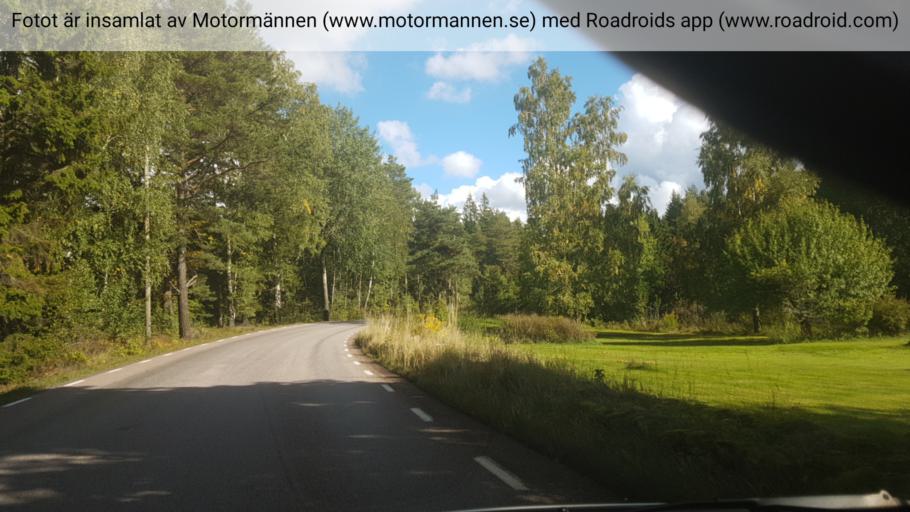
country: SE
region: Vaestra Goetaland
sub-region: Skovde Kommun
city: Stopen
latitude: 58.5373
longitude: 13.7225
